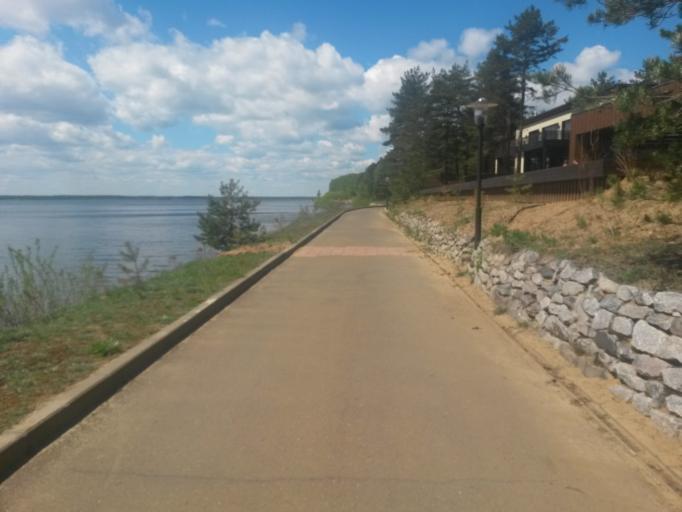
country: RU
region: Jaroslavl
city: Borok
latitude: 58.0618
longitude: 38.3484
